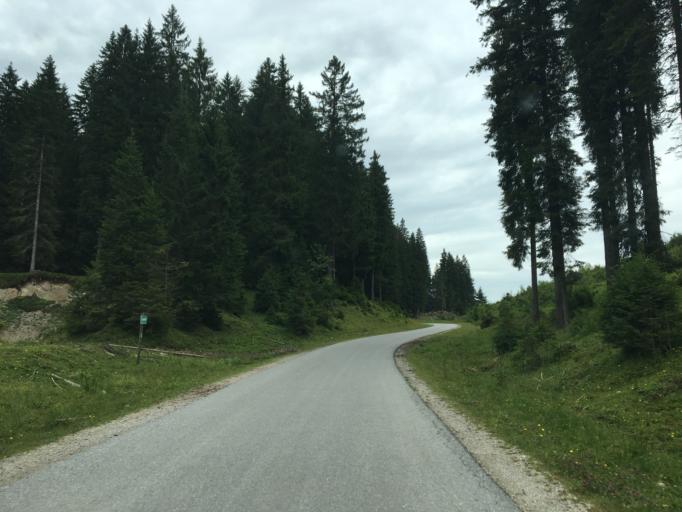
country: AT
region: Salzburg
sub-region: Politischer Bezirk Salzburg-Umgebung
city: Strobl
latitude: 47.6429
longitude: 13.4213
